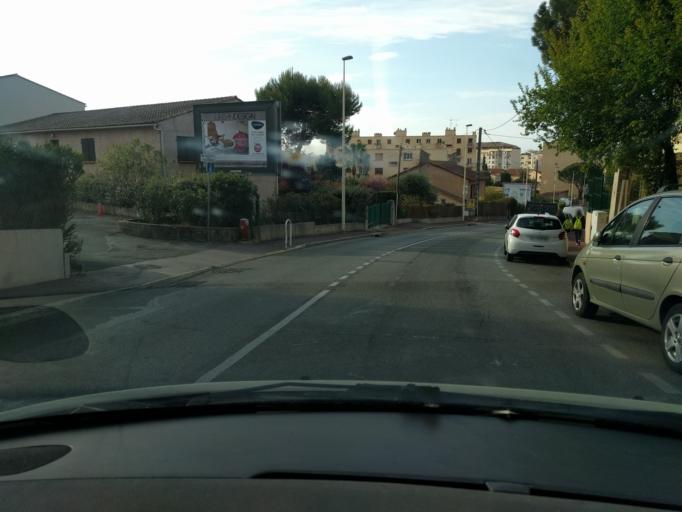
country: FR
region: Provence-Alpes-Cote d'Azur
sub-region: Departement des Alpes-Maritimes
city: Cannes
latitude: 43.5563
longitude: 6.9733
